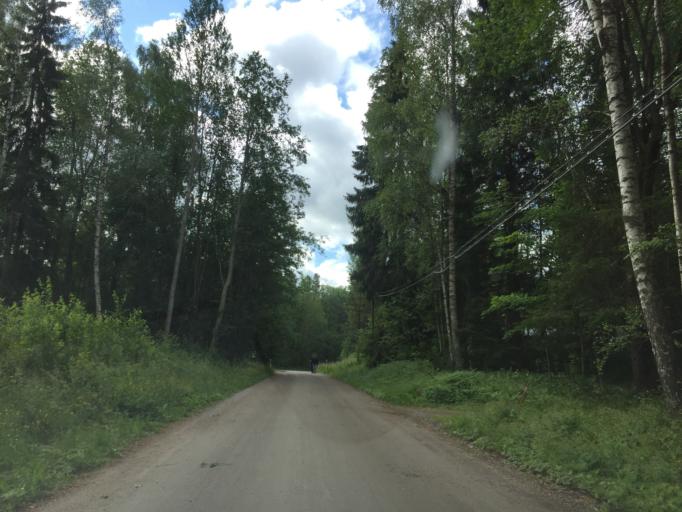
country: SE
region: OErebro
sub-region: Lekebergs Kommun
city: Fjugesta
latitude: 59.2702
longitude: 14.7964
